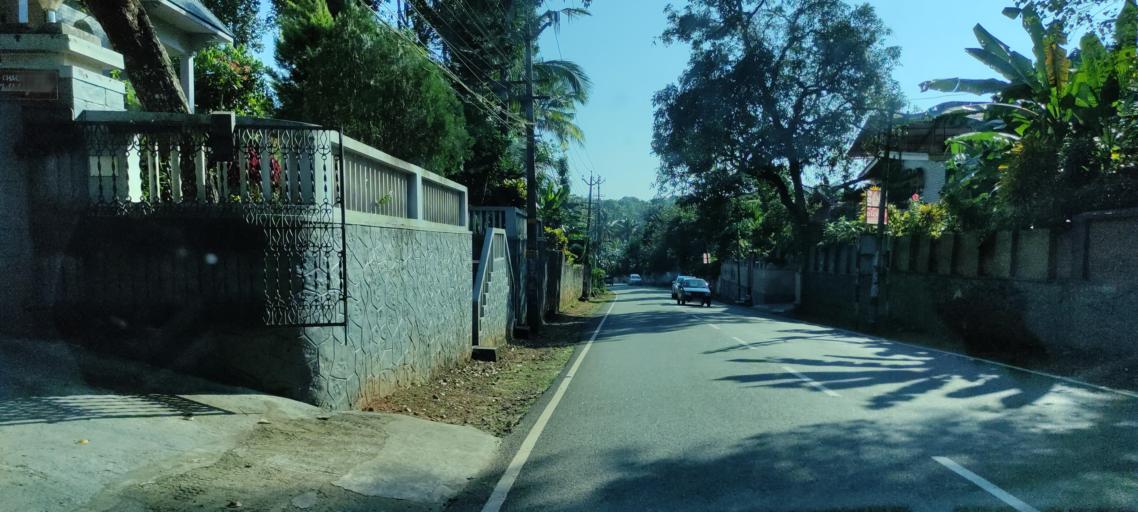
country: IN
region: Kerala
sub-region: Pattanamtitta
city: Pathanamthitta
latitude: 9.2279
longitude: 76.7541
